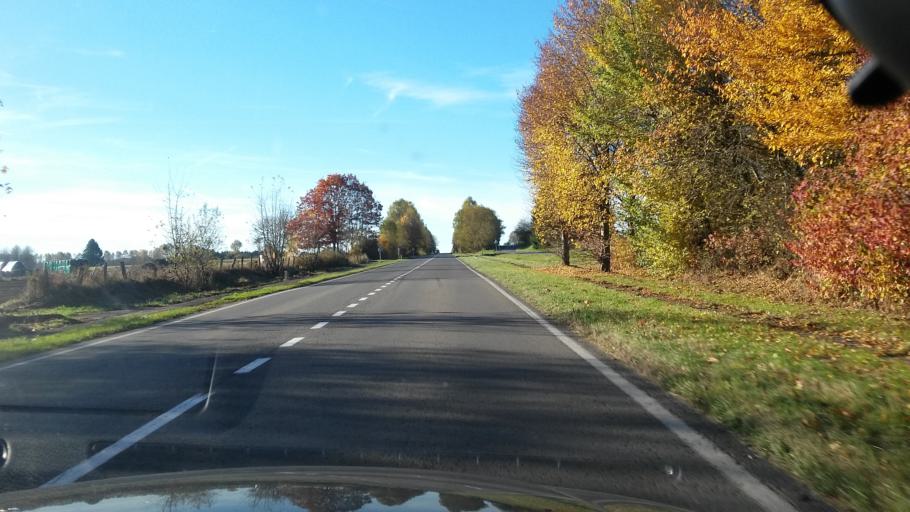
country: BE
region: Wallonia
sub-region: Province du Luxembourg
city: Saint-Leger
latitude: 49.6693
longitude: 5.6604
